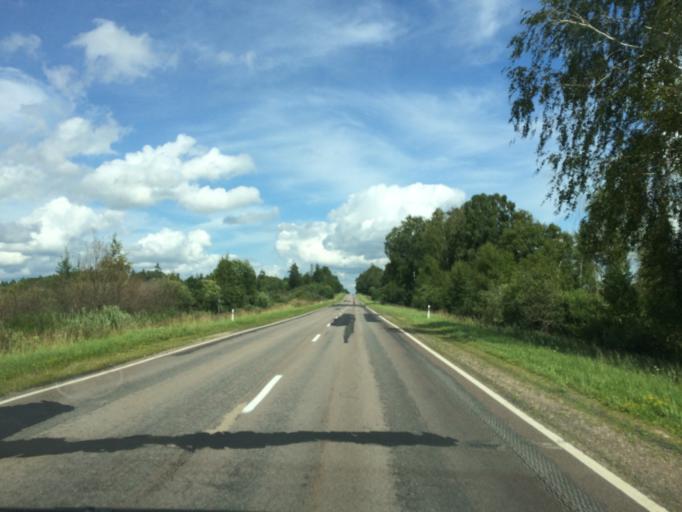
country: LV
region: Rezekne
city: Rezekne
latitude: 56.6494
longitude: 27.4946
